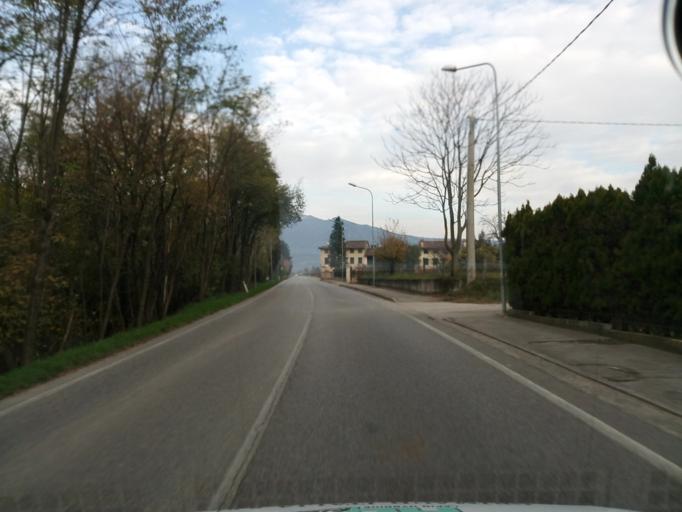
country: IT
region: Veneto
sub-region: Provincia di Treviso
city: Castelcucco
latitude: 45.8134
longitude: 11.8878
